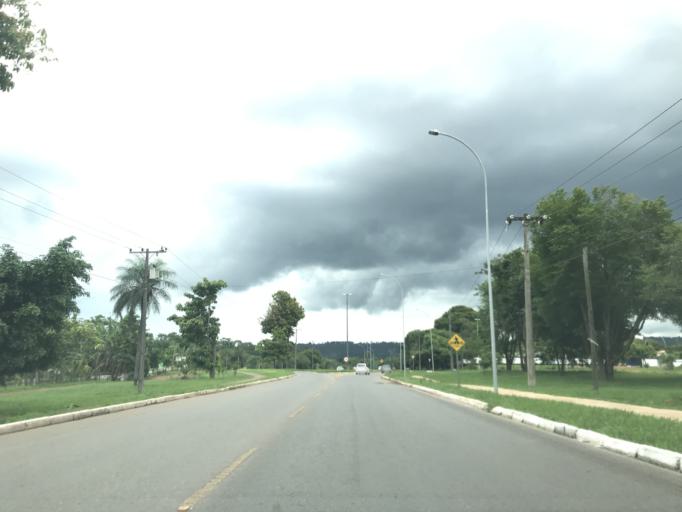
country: BR
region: Federal District
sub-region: Brasilia
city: Brasilia
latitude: -15.6512
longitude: -47.8135
